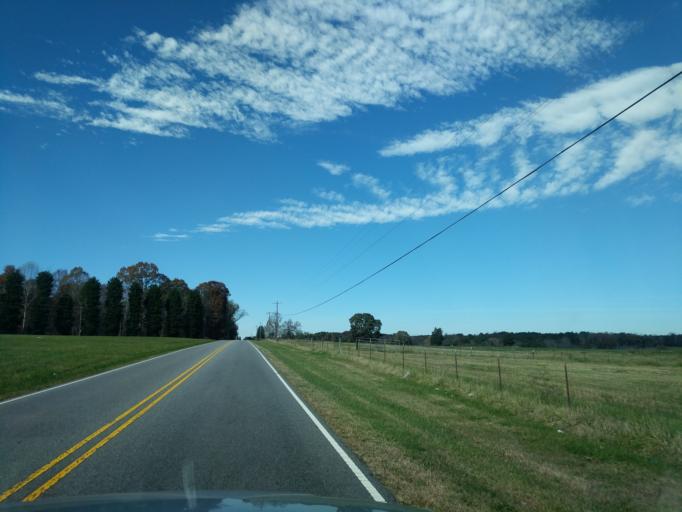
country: US
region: North Carolina
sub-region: Catawba County
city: Newton
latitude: 35.6213
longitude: -81.2593
